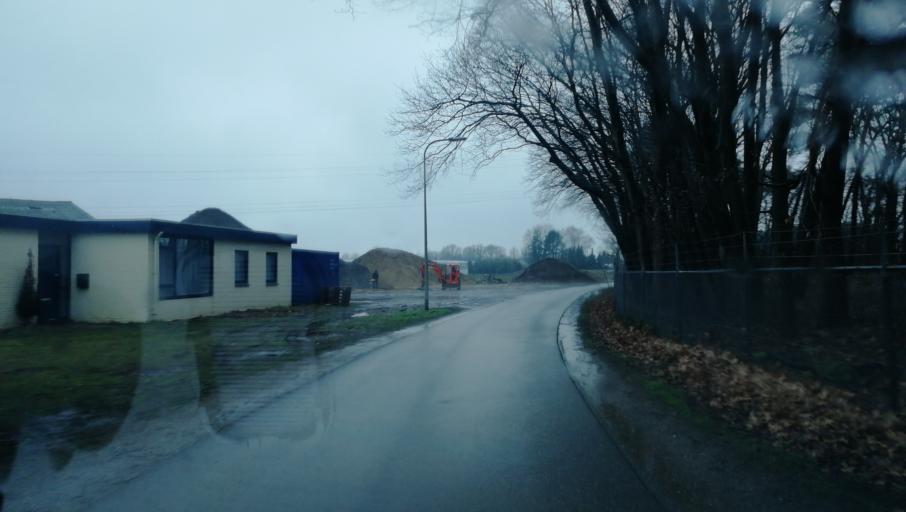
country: NL
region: Limburg
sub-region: Gemeente Venlo
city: Tegelen
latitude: 51.3464
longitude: 6.1020
